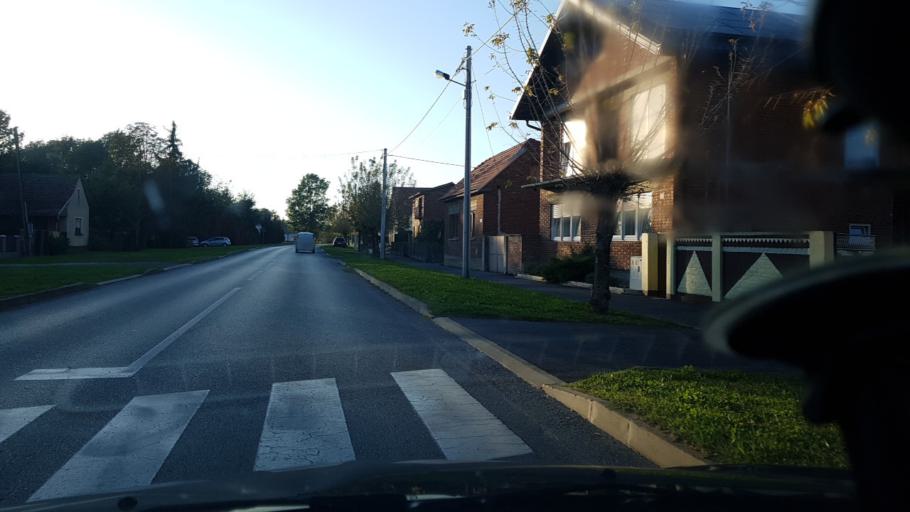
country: HR
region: Koprivnicko-Krizevacka
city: Virje
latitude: 46.0472
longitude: 17.0496
